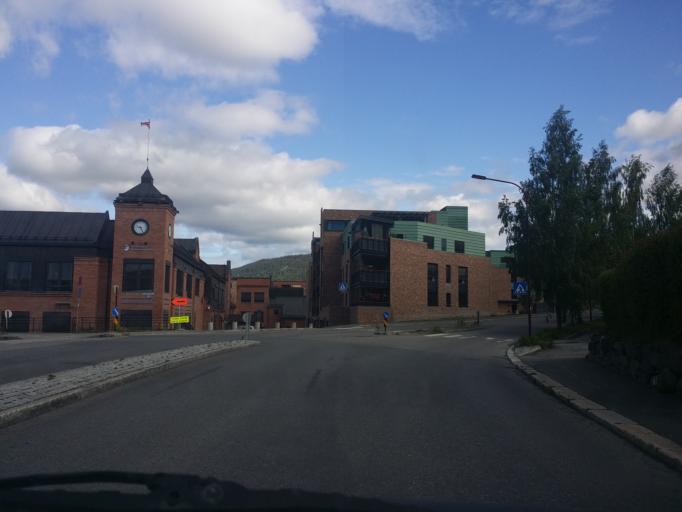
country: NO
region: Oppland
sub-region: Lillehammer
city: Lillehammer
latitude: 61.1158
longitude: 10.4685
